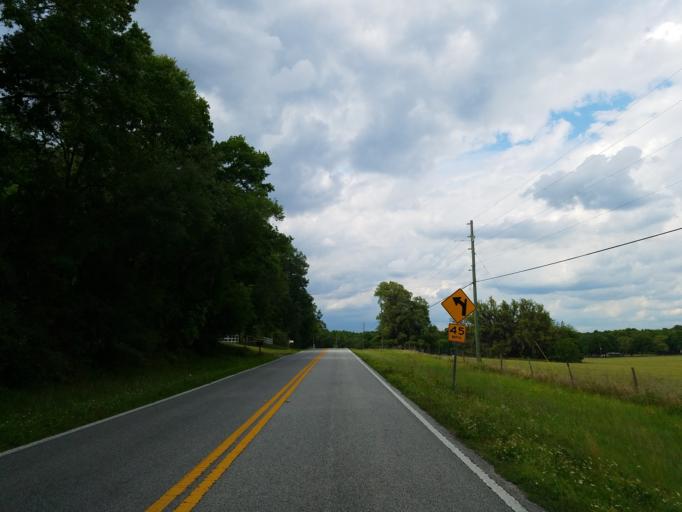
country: US
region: Florida
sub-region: Hernando County
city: Hill 'n Dale
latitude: 28.5499
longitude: -82.3009
